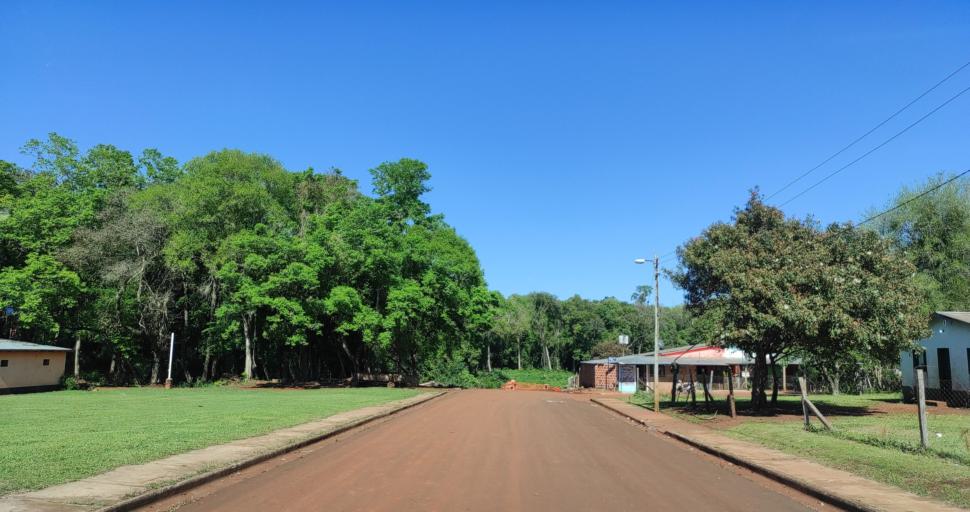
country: AR
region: Misiones
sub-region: Departamento de Candelaria
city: Loreto
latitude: -27.3330
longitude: -55.5236
